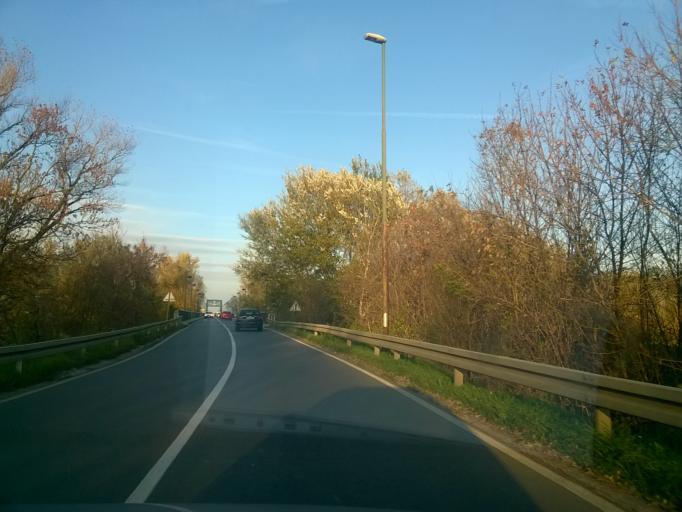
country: RS
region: Autonomna Pokrajina Vojvodina
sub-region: Juznobanatski Okrug
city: Pancevo
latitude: 44.8689
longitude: 20.6288
